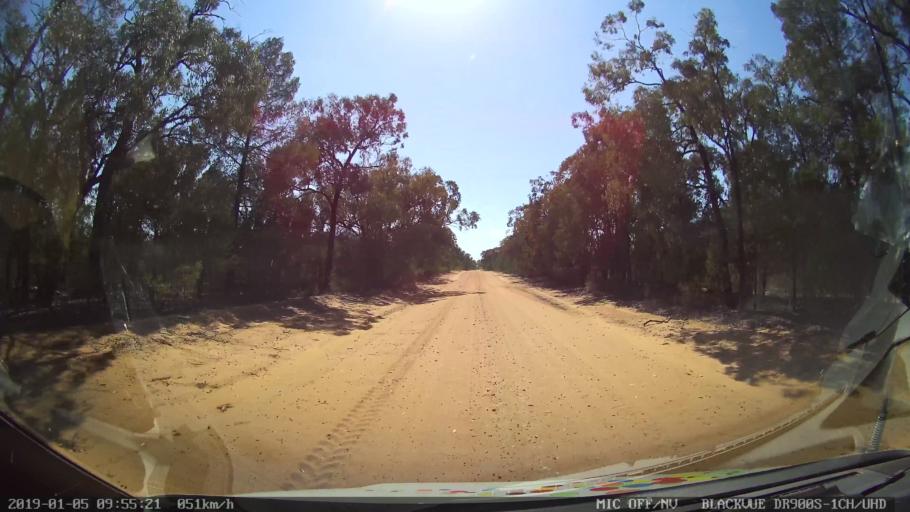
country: AU
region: New South Wales
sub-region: Gilgandra
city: Gilgandra
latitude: -31.6639
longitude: 148.7869
